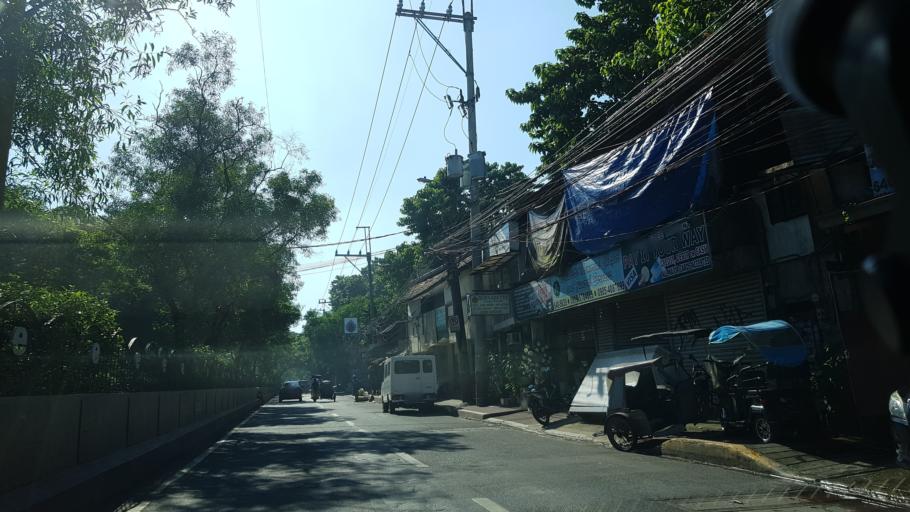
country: PH
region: Metro Manila
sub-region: Pasig
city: Pasig City
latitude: 14.5698
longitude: 121.0828
